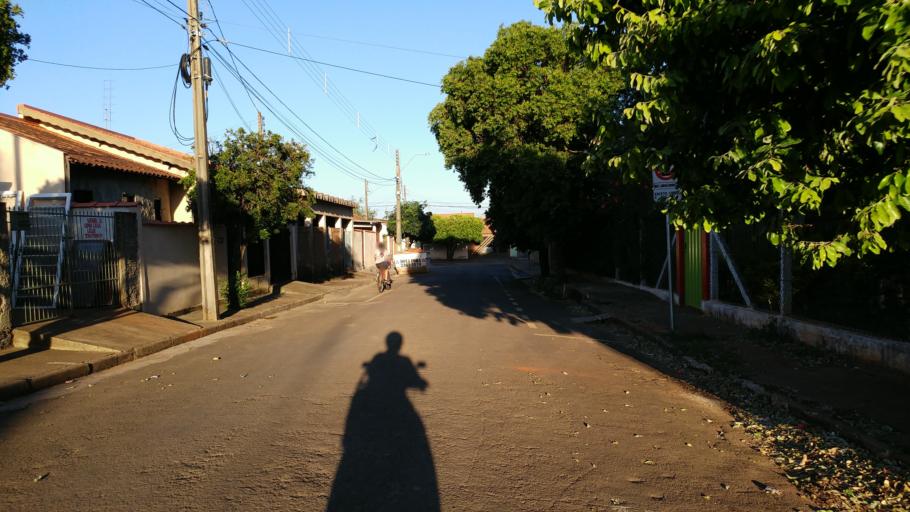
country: BR
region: Sao Paulo
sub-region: Paraguacu Paulista
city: Paraguacu Paulista
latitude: -22.4333
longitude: -50.5827
